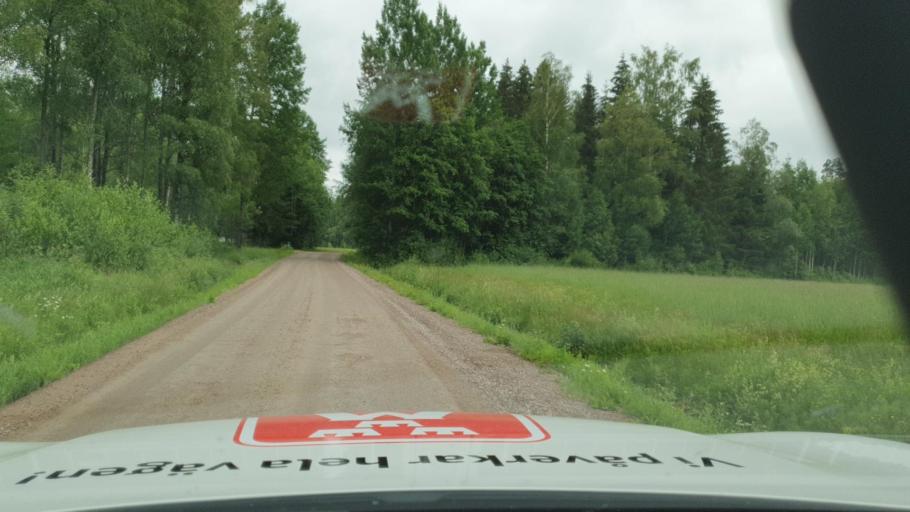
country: SE
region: Vaermland
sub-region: Filipstads Kommun
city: Filipstad
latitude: 59.5367
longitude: 13.9689
